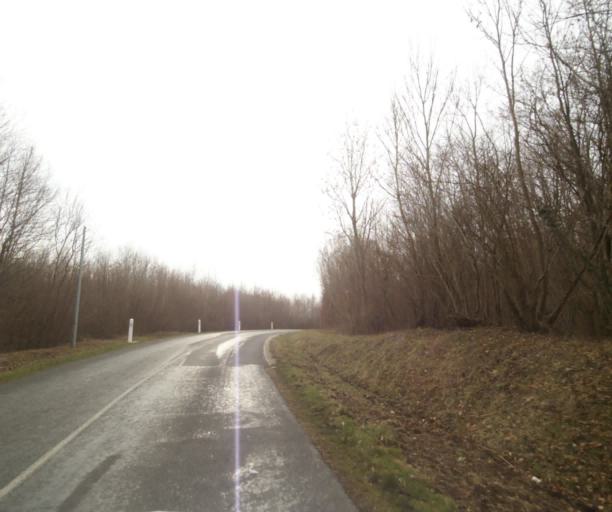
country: FR
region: Champagne-Ardenne
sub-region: Departement de la Haute-Marne
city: Villiers-en-Lieu
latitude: 48.6940
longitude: 4.8925
